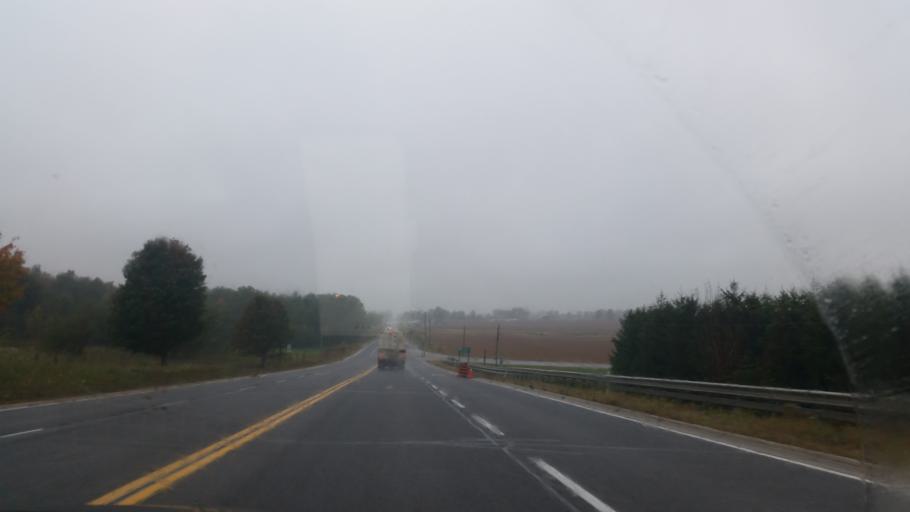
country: CA
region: Ontario
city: London
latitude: 43.1706
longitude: -81.3412
